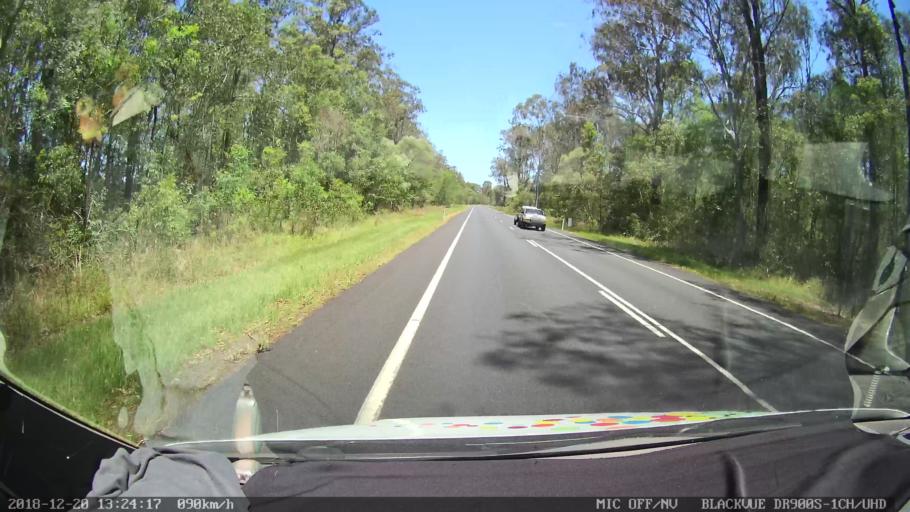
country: AU
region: New South Wales
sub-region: Richmond Valley
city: Casino
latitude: -29.1154
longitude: 153.0002
